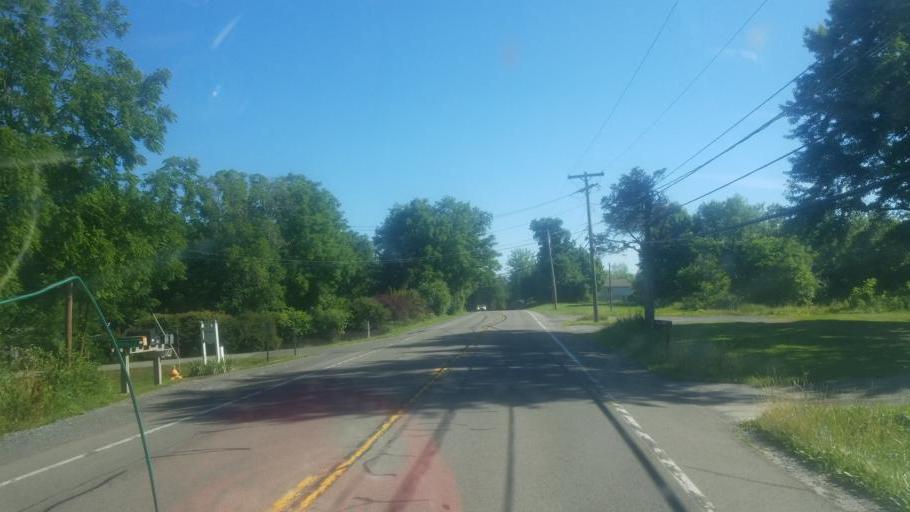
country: US
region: New York
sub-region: Ontario County
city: Canandaigua
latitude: 42.8558
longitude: -77.2527
